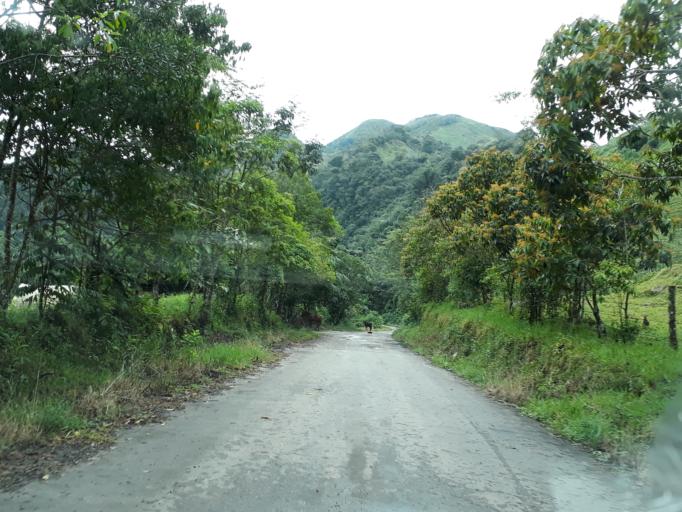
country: CO
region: Boyaca
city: Santa Maria
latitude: 4.7424
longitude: -73.3080
